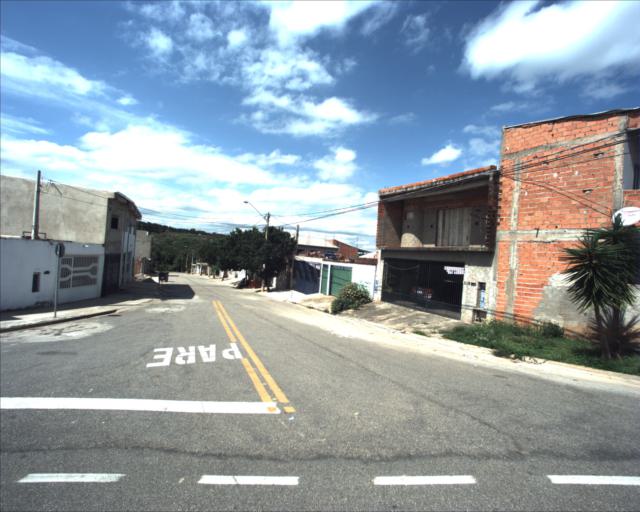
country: BR
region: Sao Paulo
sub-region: Sorocaba
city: Sorocaba
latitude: -23.3908
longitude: -47.3796
